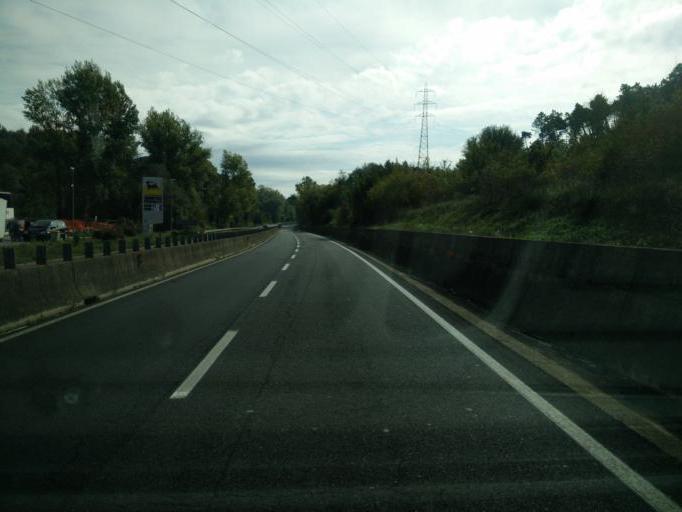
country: IT
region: Tuscany
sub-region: Provincia di Siena
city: Siena
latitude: 43.3162
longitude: 11.3046
